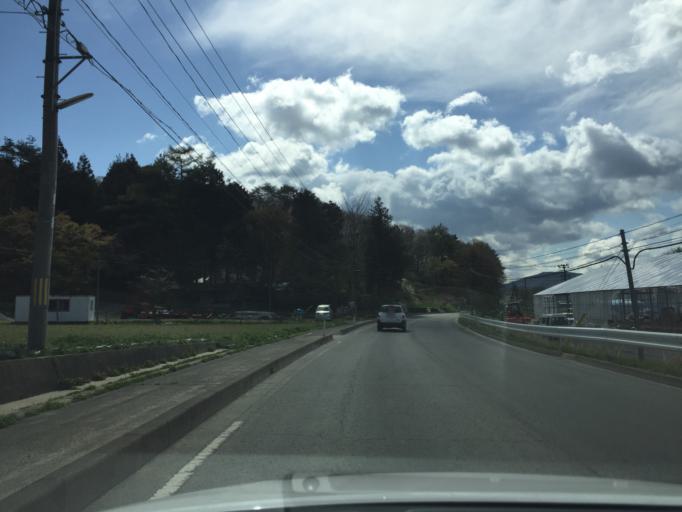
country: JP
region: Fukushima
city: Funehikimachi-funehiki
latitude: 37.6092
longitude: 140.6640
